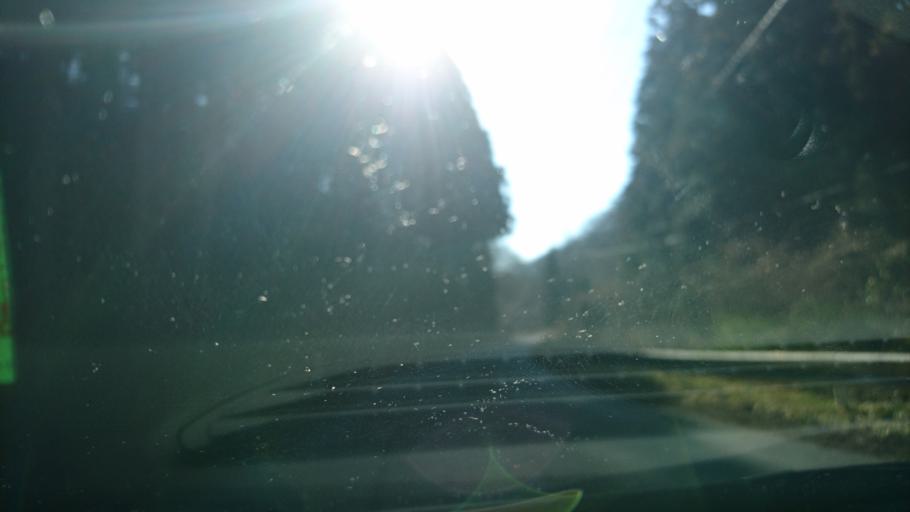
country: JP
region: Iwate
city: Ichinoseki
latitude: 38.8143
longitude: 141.3003
